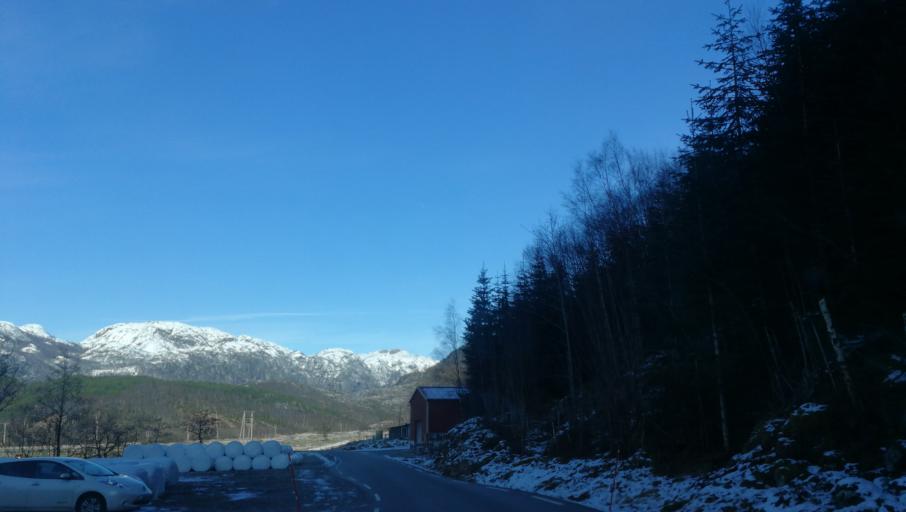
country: NO
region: Rogaland
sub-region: Hjelmeland
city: Hjelmelandsvagen
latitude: 59.1281
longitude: 6.2753
